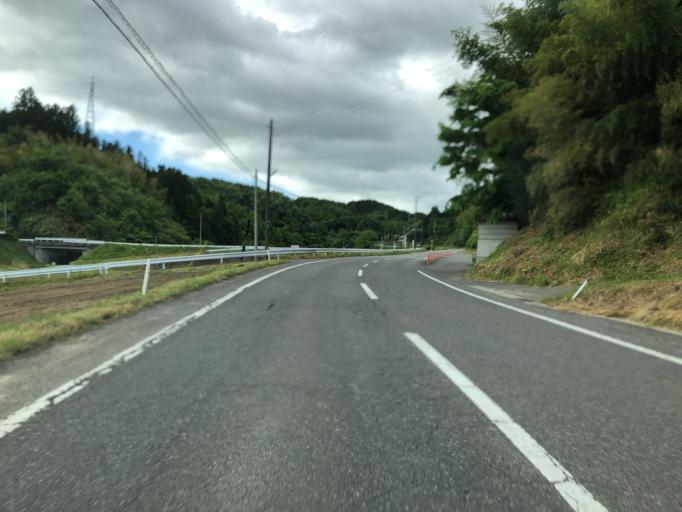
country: JP
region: Fukushima
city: Nihommatsu
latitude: 37.5444
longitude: 140.4602
